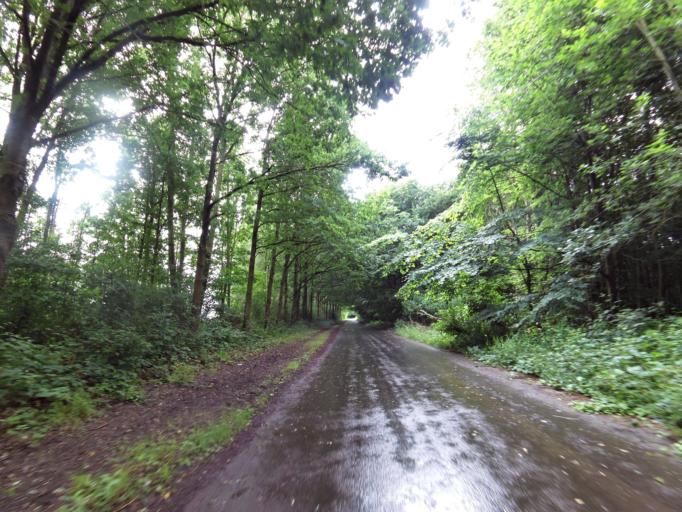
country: NL
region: Limburg
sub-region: Gemeente Kerkrade
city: Kerkrade
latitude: 50.8790
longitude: 6.0345
